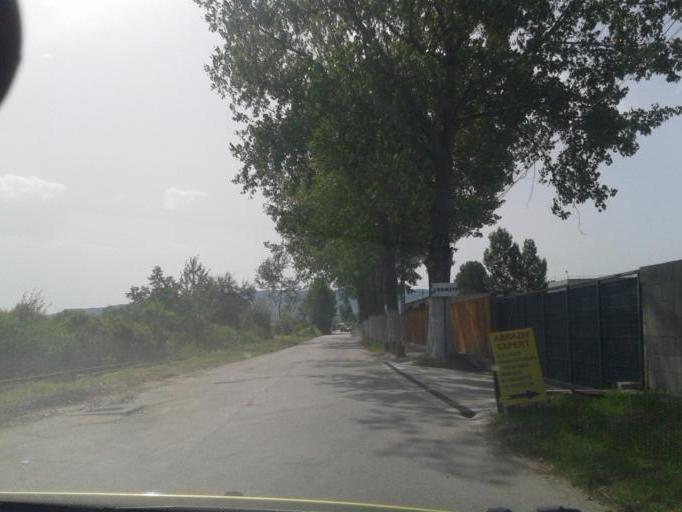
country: RO
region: Valcea
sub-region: Municipiul Ramnicu Valcea
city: Copacelu
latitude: 45.0688
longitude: 24.3287
